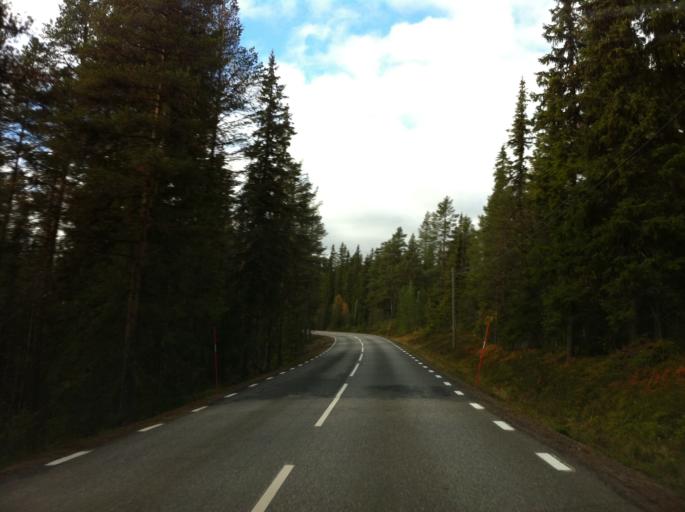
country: NO
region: Hedmark
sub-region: Engerdal
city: Engerdal
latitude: 61.9894
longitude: 12.4628
